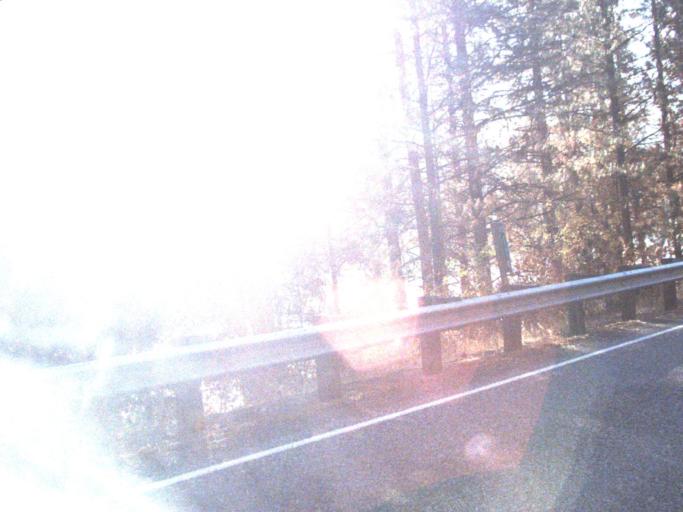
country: US
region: Washington
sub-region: Okanogan County
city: Coulee Dam
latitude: 48.0430
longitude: -118.6705
